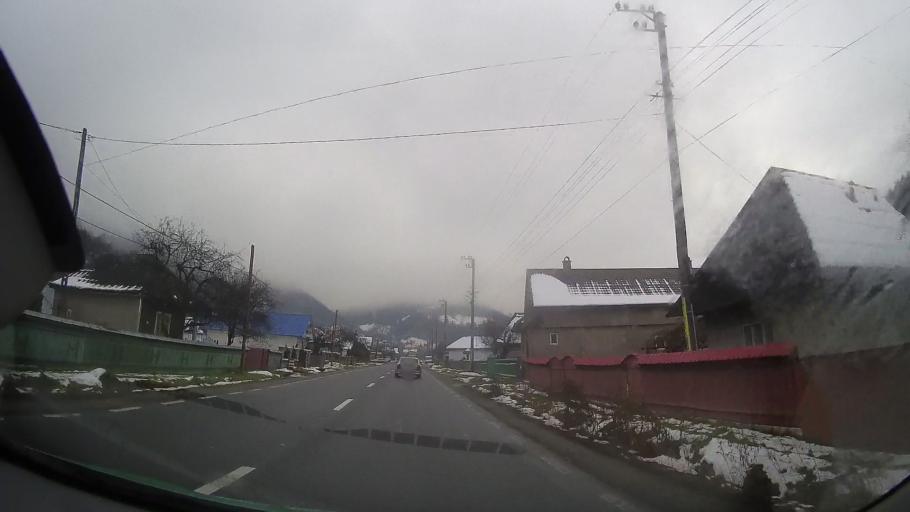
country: RO
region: Neamt
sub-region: Comuna Bicazu Ardelean
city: Bicazu Ardelean
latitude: 46.8607
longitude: 25.9368
